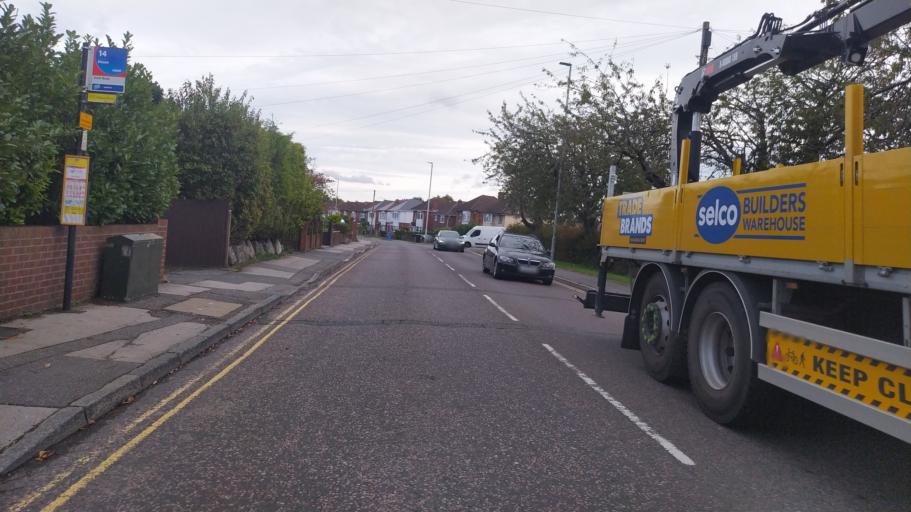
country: GB
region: England
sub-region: Dorset
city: Parkstone
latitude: 50.7483
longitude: -1.9193
